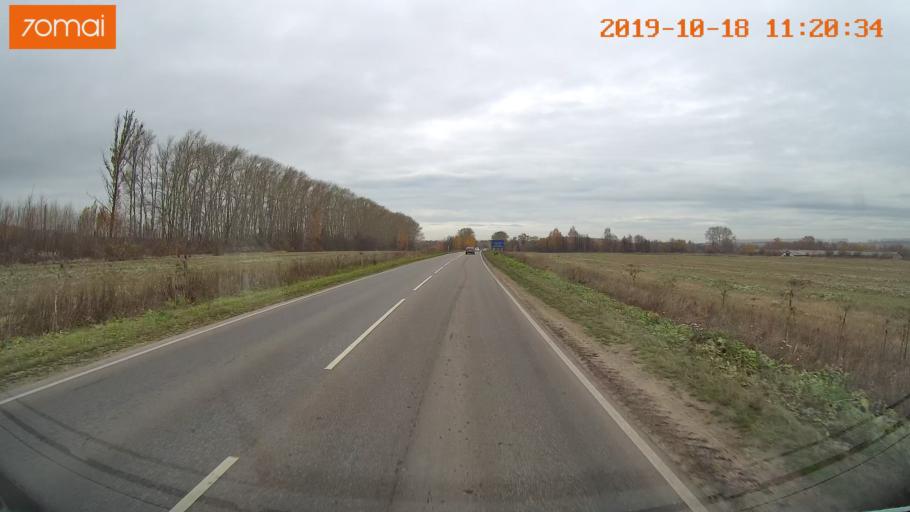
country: RU
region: Tula
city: Kimovsk
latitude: 54.0627
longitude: 38.5592
